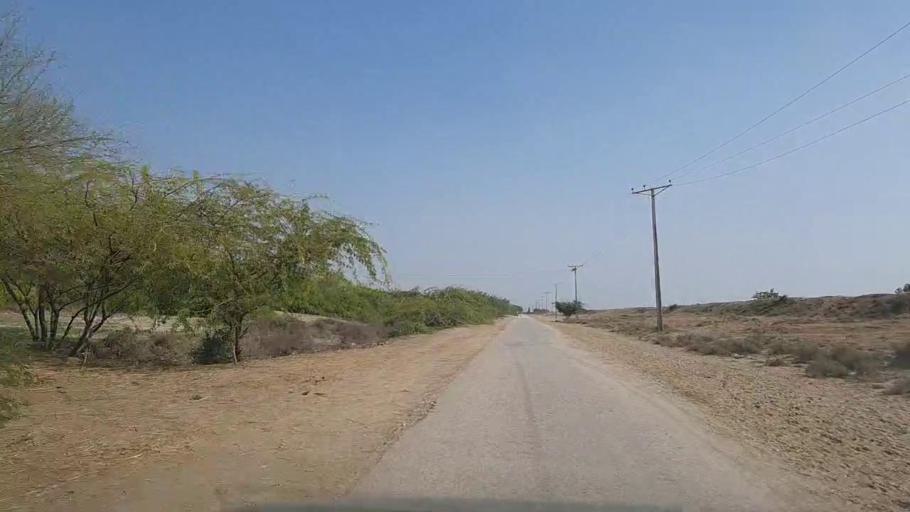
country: PK
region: Sindh
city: Thatta
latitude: 24.5834
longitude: 67.9186
